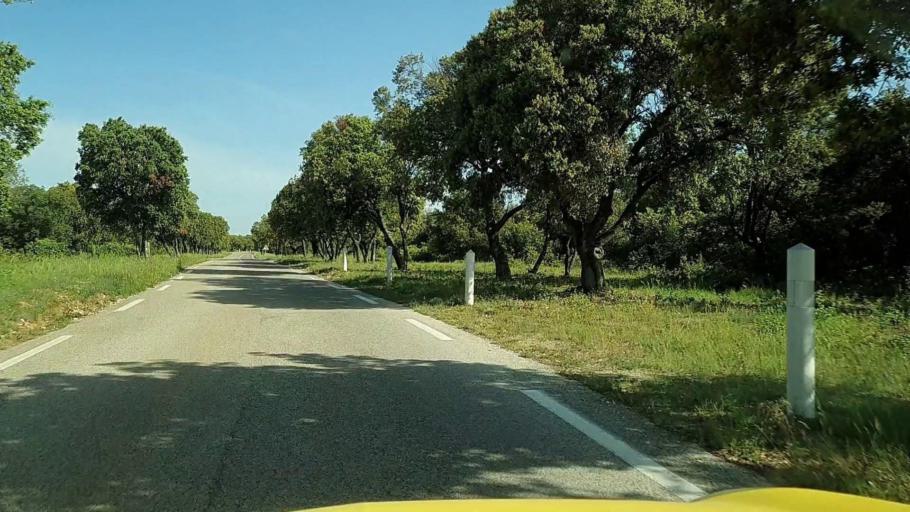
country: FR
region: Languedoc-Roussillon
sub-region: Departement du Gard
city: Montaren-et-Saint-Mediers
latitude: 44.1008
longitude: 4.3874
